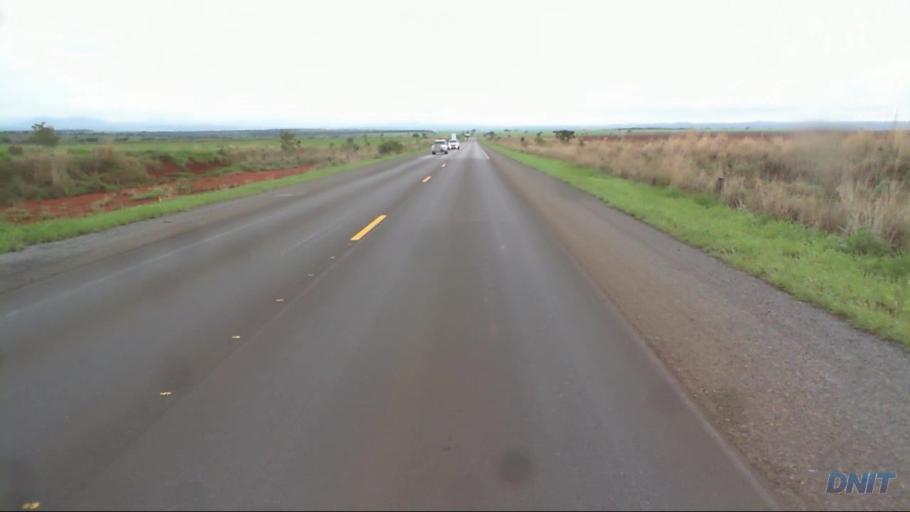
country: BR
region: Goias
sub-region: Padre Bernardo
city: Padre Bernardo
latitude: -15.1744
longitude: -48.3983
